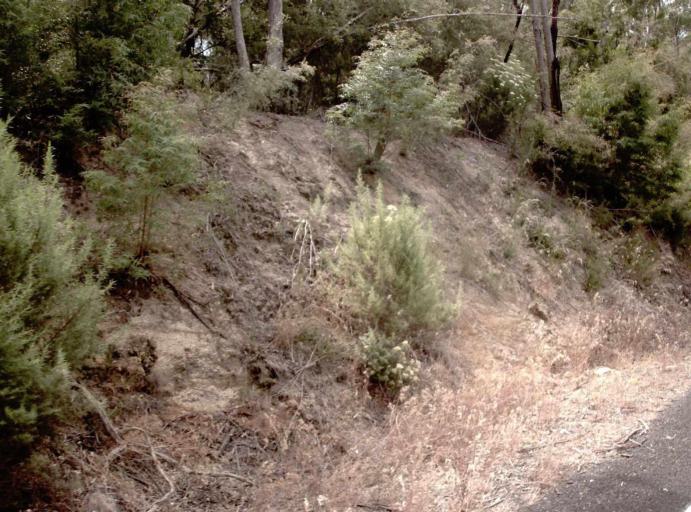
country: AU
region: New South Wales
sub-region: Bega Valley
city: Eden
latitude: -37.4660
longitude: 149.5875
